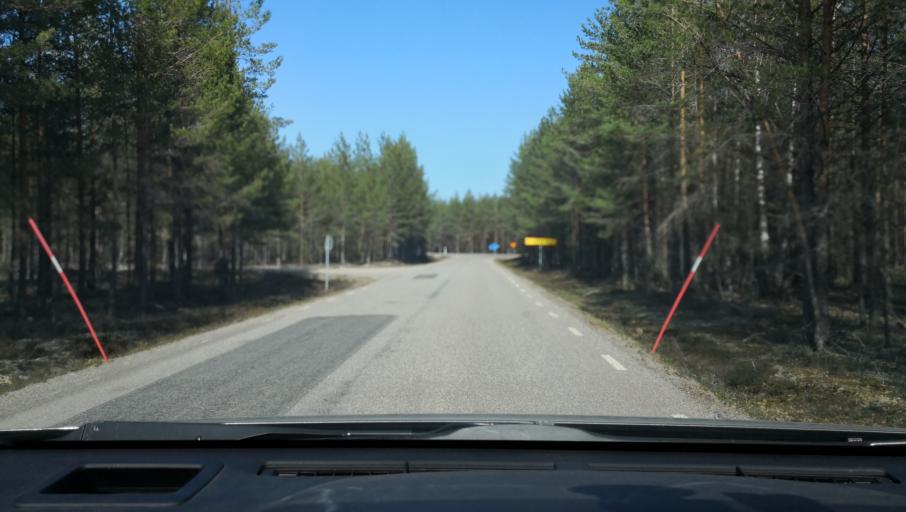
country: SE
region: Uppsala
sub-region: Heby Kommun
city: Heby
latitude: 60.0506
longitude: 16.8644
